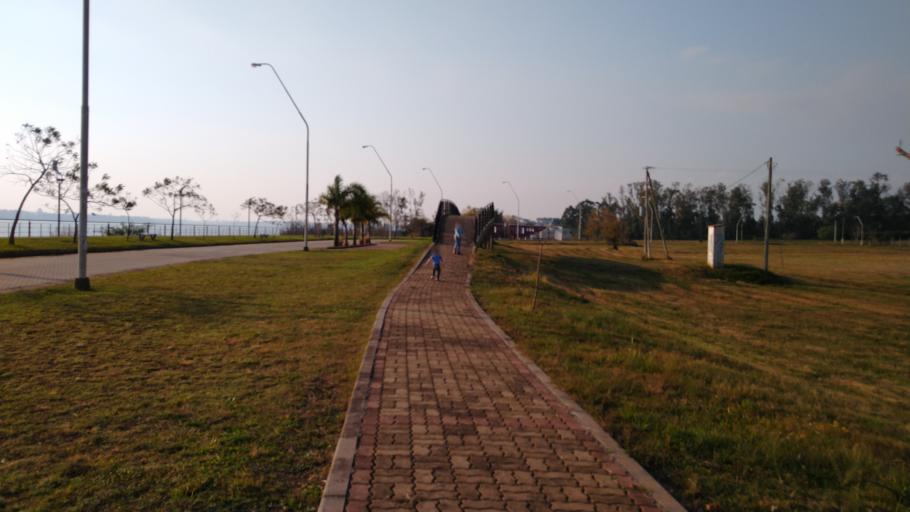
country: AR
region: Entre Rios
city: Santa Ana
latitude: -30.8989
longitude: -57.9365
